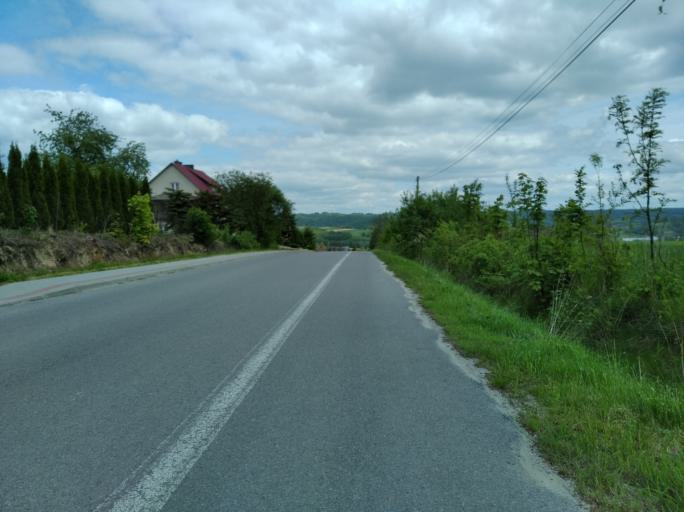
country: PL
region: Subcarpathian Voivodeship
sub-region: Powiat ropczycko-sedziszowski
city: Wielopole Skrzynskie
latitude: 49.9405
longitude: 21.6059
